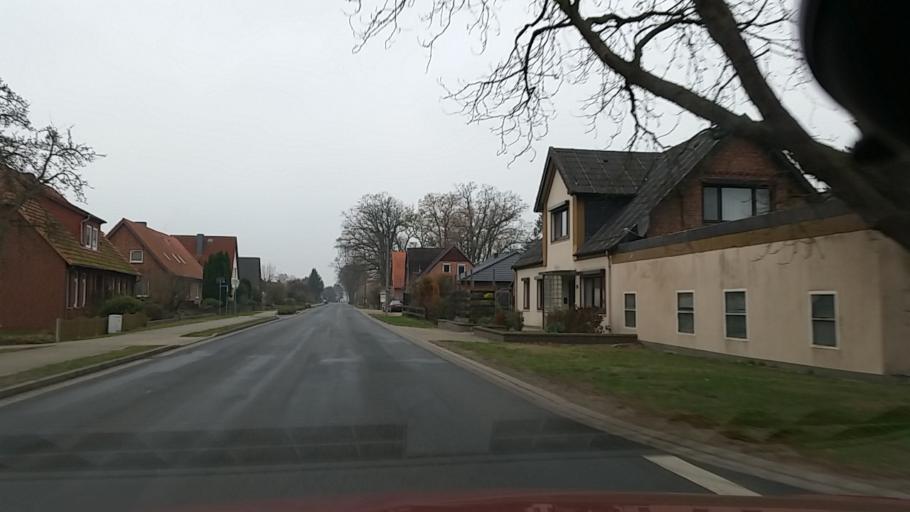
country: DE
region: Lower Saxony
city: Wittingen
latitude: 52.7296
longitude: 10.7080
